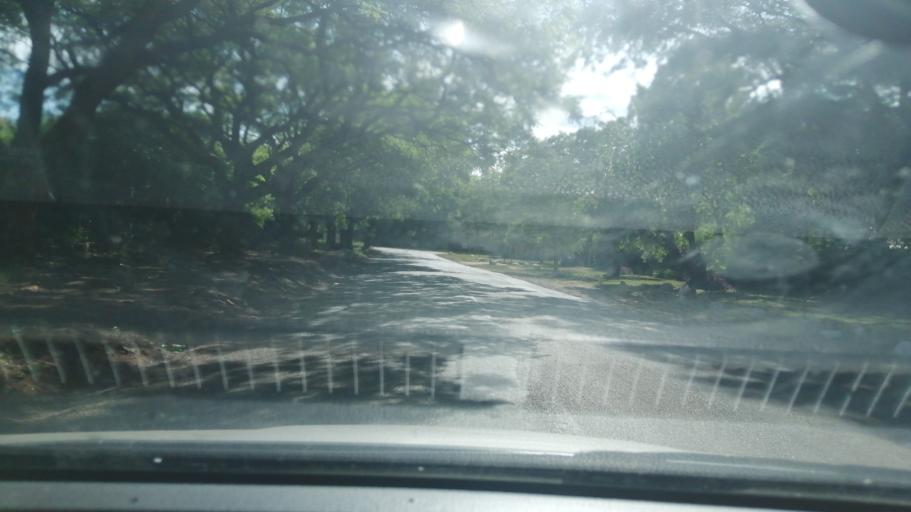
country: ZW
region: Harare
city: Harare
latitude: -17.7961
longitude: 31.0525
